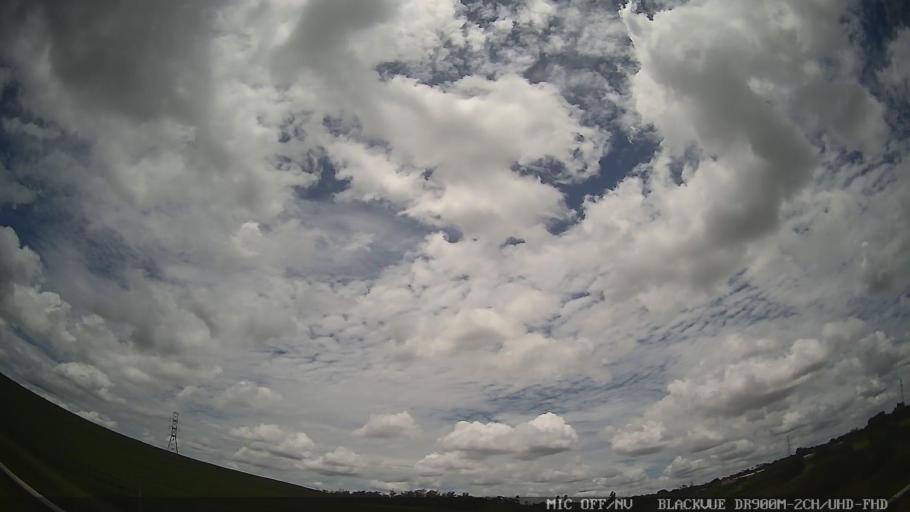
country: BR
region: Sao Paulo
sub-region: Jaguariuna
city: Jaguariuna
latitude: -22.7836
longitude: -47.0274
